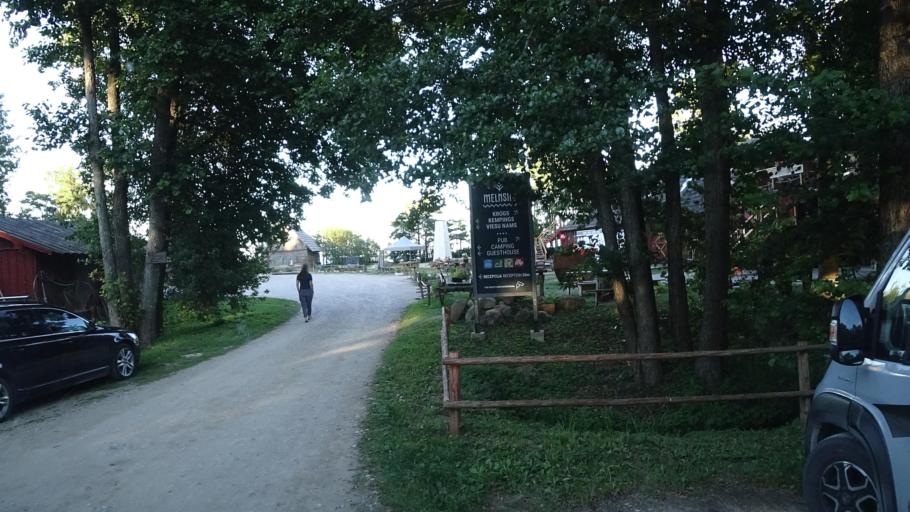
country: LV
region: Dundaga
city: Dundaga
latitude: 57.6507
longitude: 22.5807
